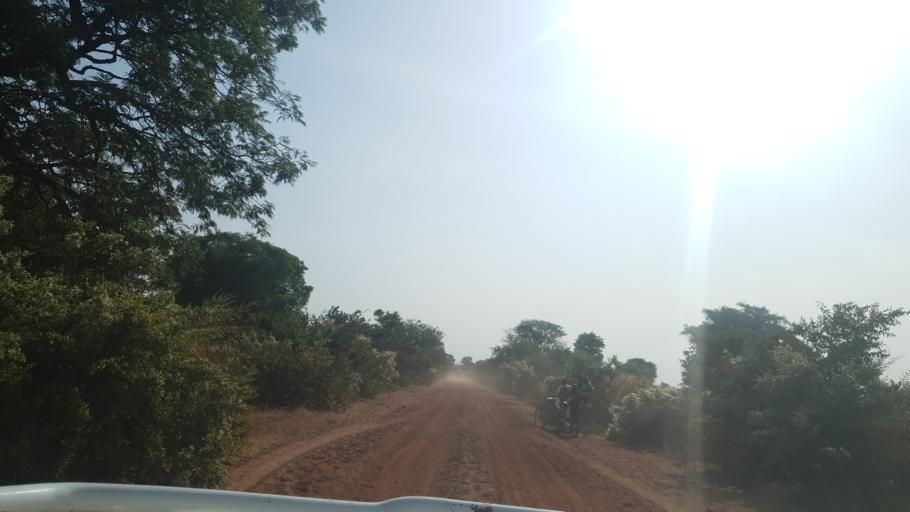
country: ML
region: Koulikoro
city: Dioila
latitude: 12.7088
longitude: -6.7806
